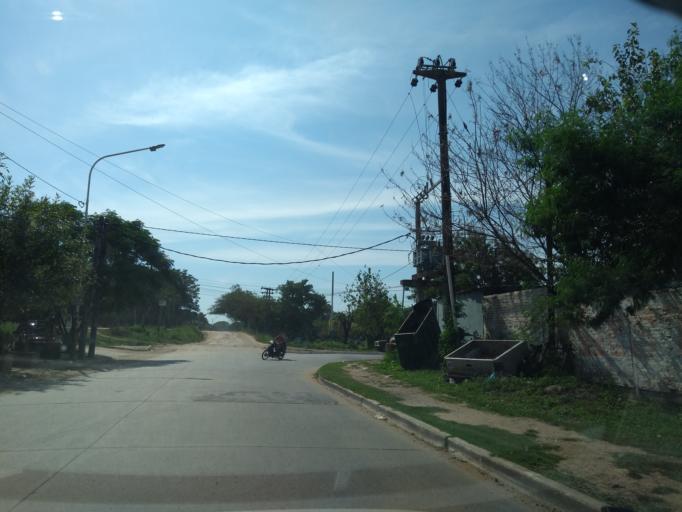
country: AR
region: Chaco
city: Barranqueras
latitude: -27.4633
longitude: -58.9524
